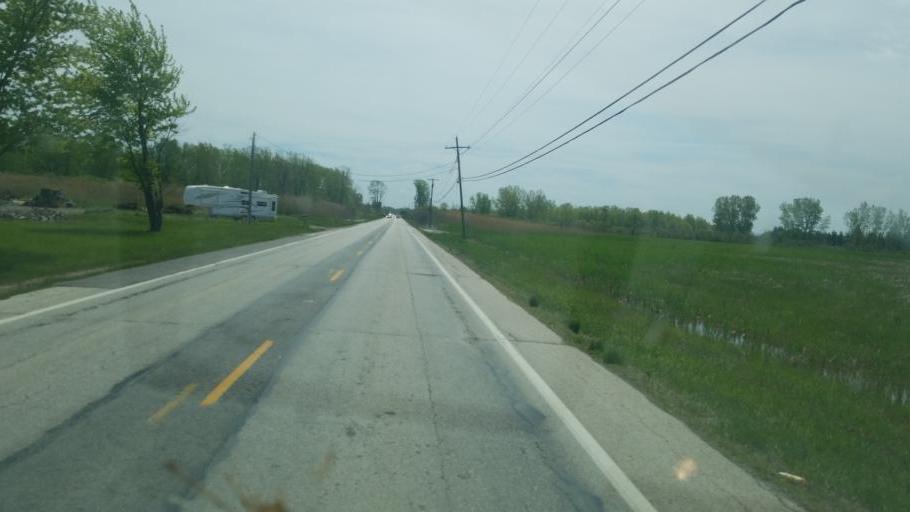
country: US
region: Ohio
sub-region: Ottawa County
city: Oak Harbor
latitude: 41.5736
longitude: -83.0861
